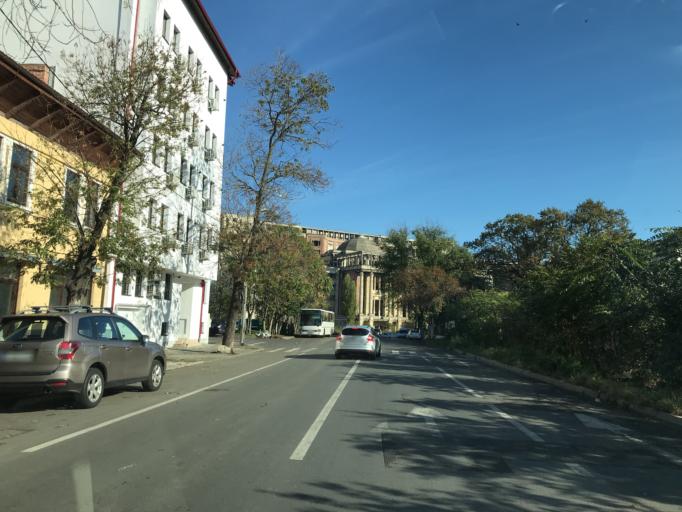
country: RO
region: Bucuresti
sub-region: Municipiul Bucuresti
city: Bucuresti
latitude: 44.4204
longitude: 26.0850
